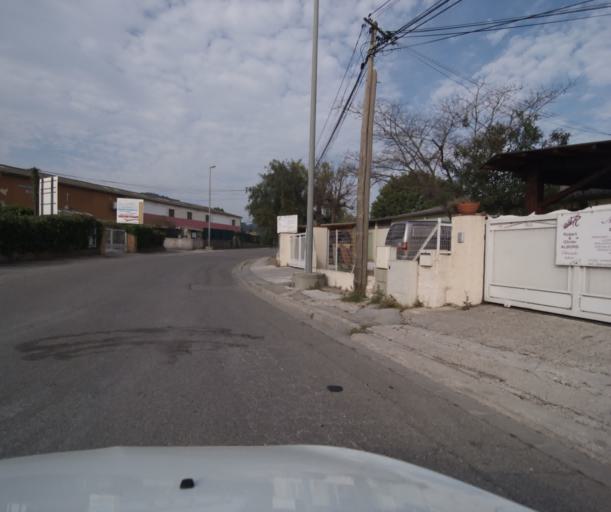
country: FR
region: Provence-Alpes-Cote d'Azur
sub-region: Departement du Var
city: Hyeres
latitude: 43.1115
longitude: 6.1099
